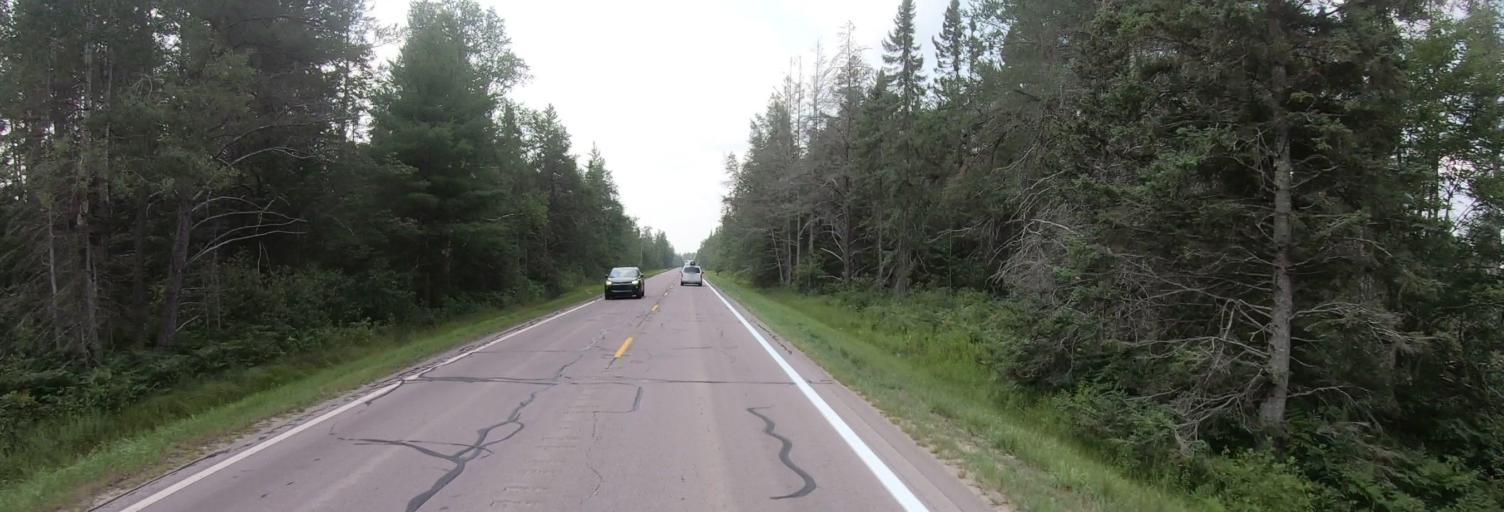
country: US
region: Michigan
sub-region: Luce County
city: Newberry
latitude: 46.4690
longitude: -85.4312
